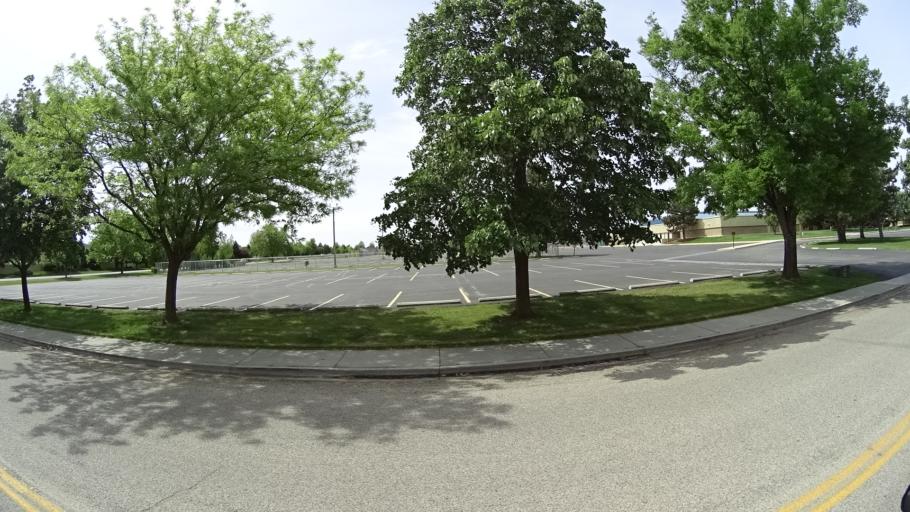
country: US
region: Idaho
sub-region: Ada County
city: Meridian
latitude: 43.5539
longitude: -116.3251
